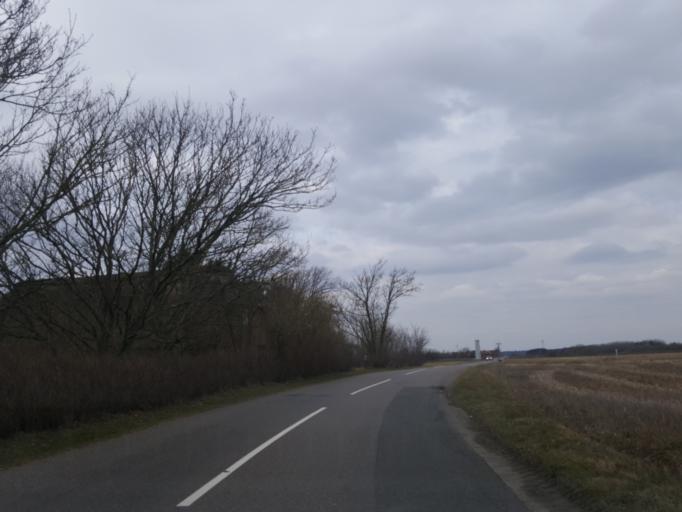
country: DK
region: Central Jutland
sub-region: Lemvig Kommune
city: Lemvig
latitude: 56.4175
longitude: 8.2329
